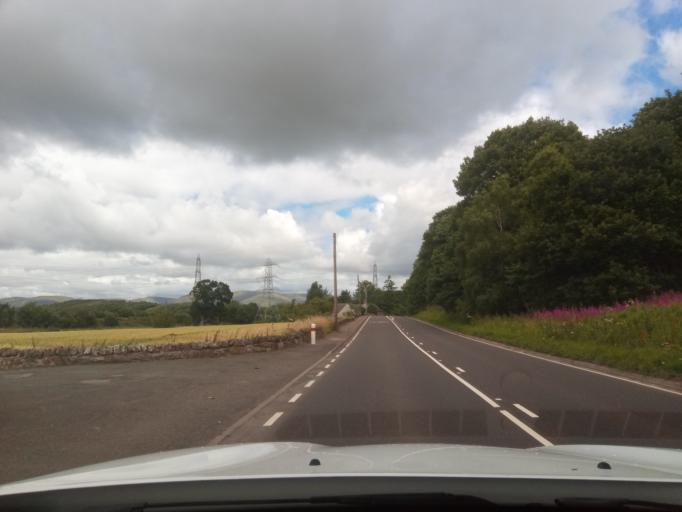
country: GB
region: Scotland
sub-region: Fife
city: Kincardine
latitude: 56.0836
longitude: -3.7202
